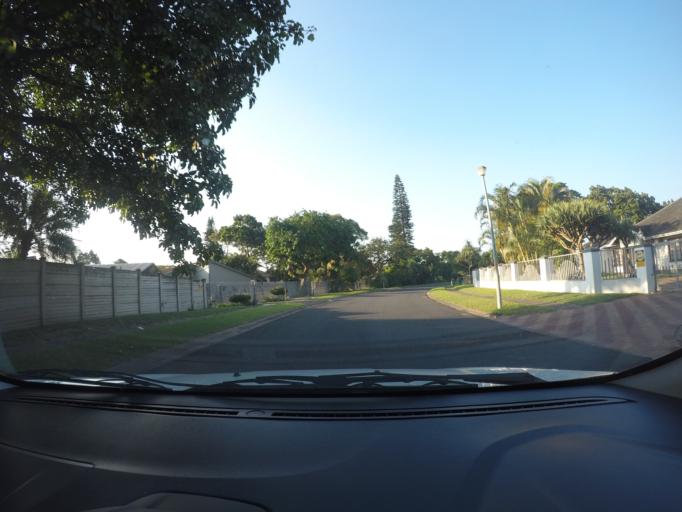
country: ZA
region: KwaZulu-Natal
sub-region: uThungulu District Municipality
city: Richards Bay
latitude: -28.7862
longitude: 32.0910
